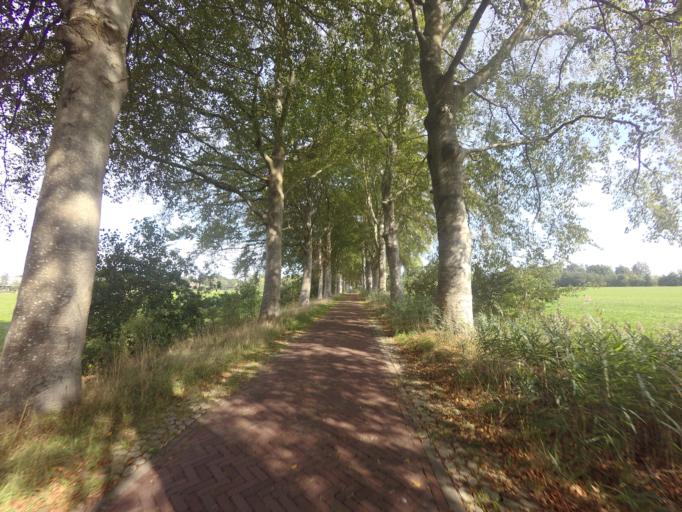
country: NL
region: Groningen
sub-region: Gemeente Leek
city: Leek
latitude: 53.1767
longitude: 6.3922
